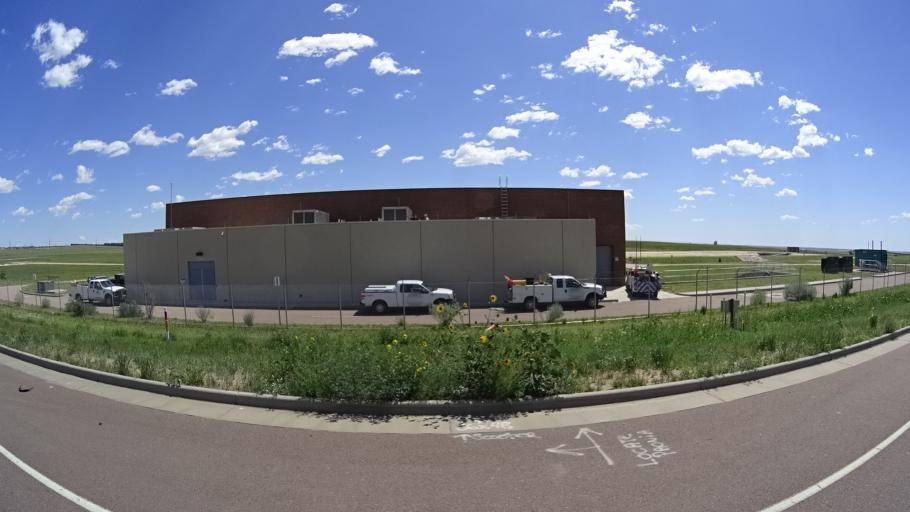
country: US
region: Colorado
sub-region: El Paso County
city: Cimarron Hills
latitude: 38.8442
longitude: -104.6828
